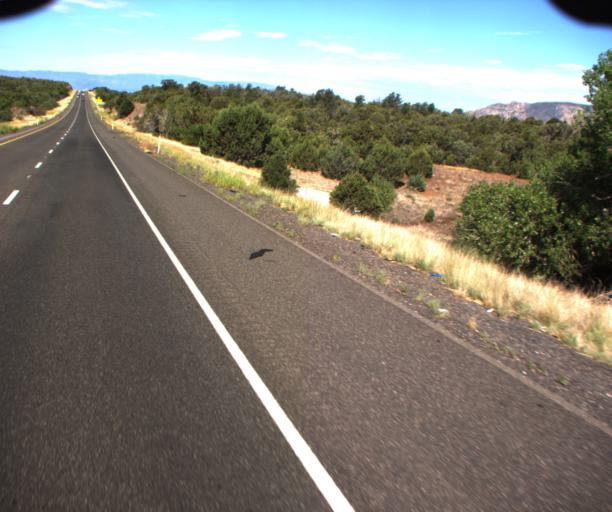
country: US
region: Arizona
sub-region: Yavapai County
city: Village of Oak Creek (Big Park)
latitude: 34.7805
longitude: -111.6209
